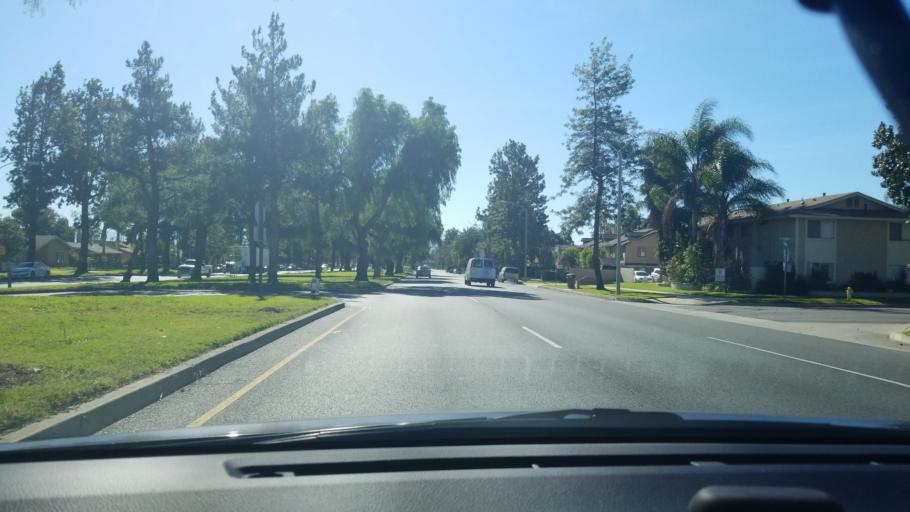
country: US
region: California
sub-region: San Bernardino County
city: Ontario
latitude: 34.0377
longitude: -117.6510
